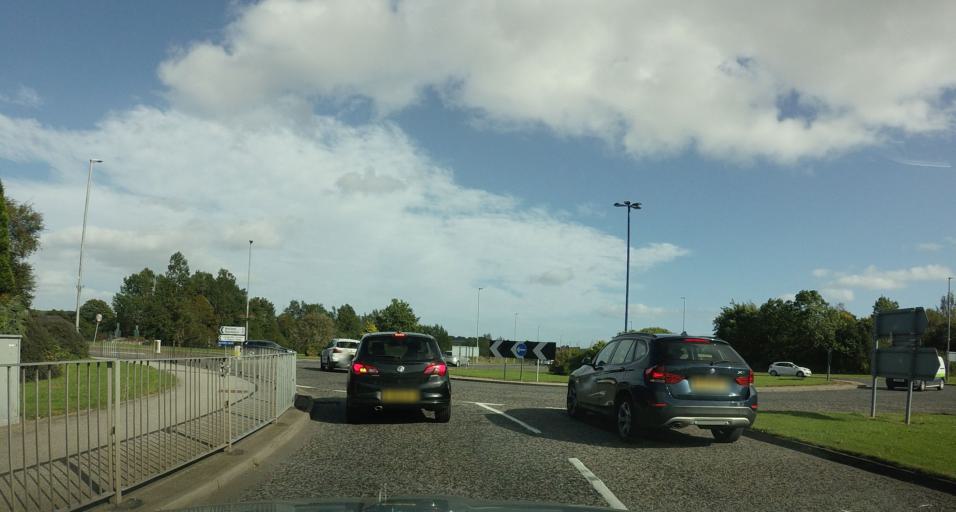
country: GB
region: Scotland
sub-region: Aberdeenshire
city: Westhill
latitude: 57.1503
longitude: -2.2740
